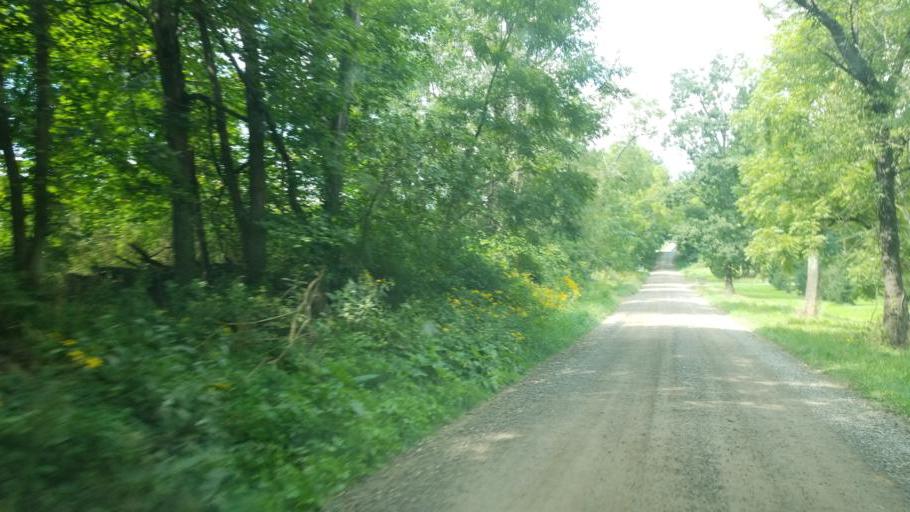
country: US
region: Ohio
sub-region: Knox County
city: Oak Hill
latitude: 40.4080
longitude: -82.2809
